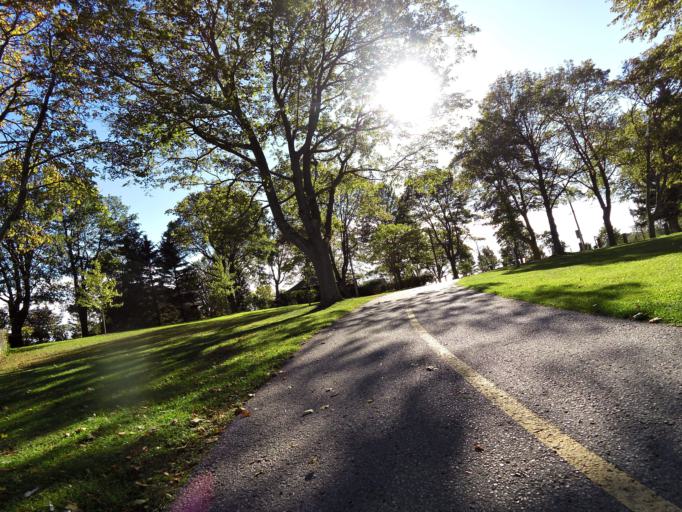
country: CA
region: Ontario
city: Oshawa
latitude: 43.8592
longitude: -78.8315
